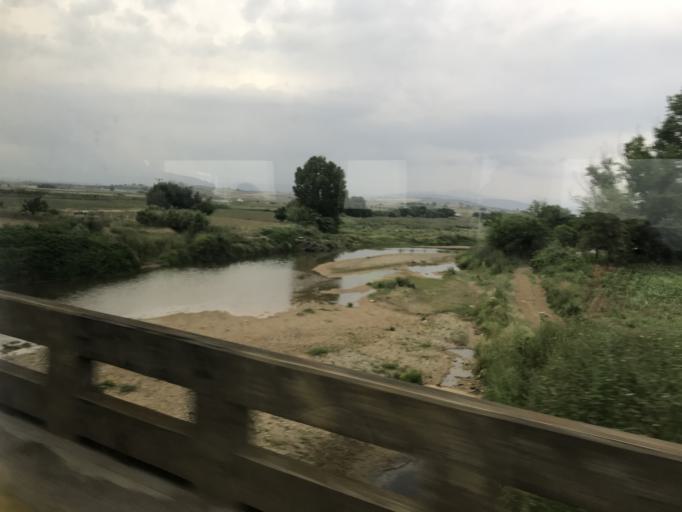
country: GR
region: East Macedonia and Thrace
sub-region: Nomos Rodopis
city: Aratos
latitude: 41.0823
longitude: 25.5478
